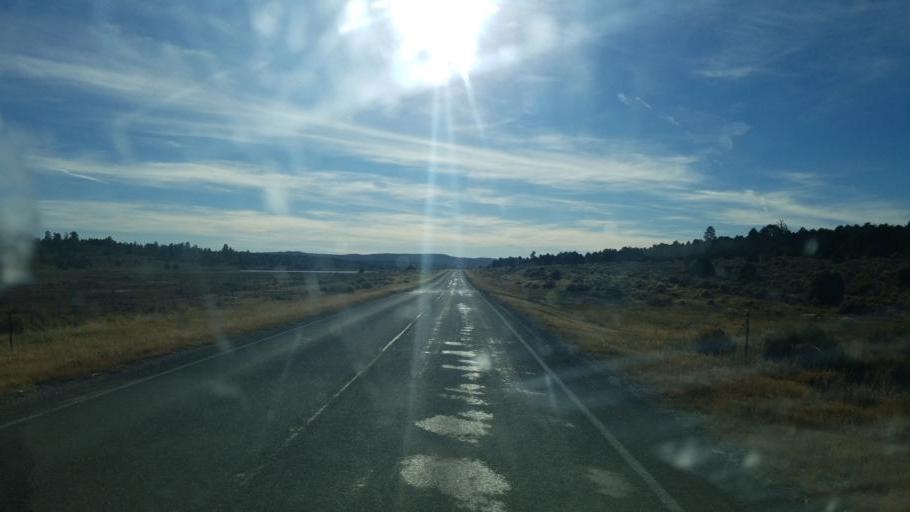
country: US
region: New Mexico
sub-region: Rio Arriba County
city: Navajo
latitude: 36.7746
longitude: -107.1578
